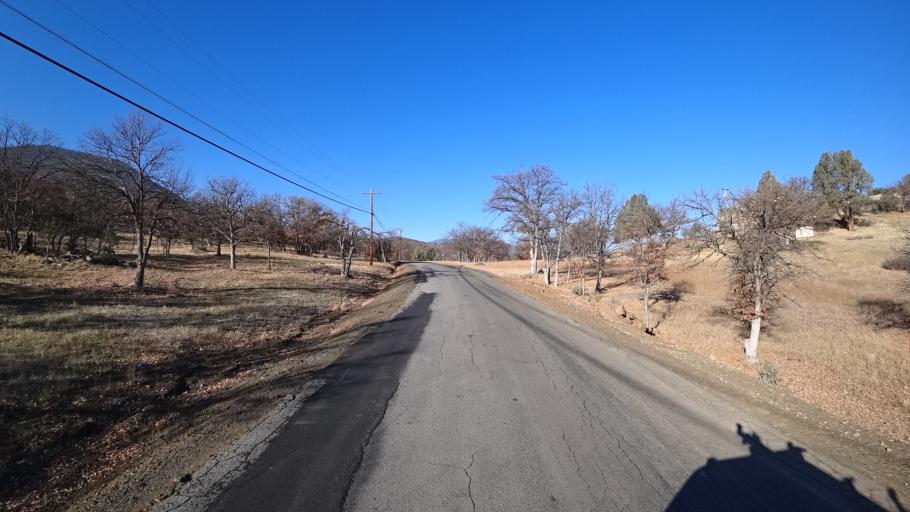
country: US
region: California
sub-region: Siskiyou County
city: Montague
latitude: 41.8884
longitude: -122.4867
